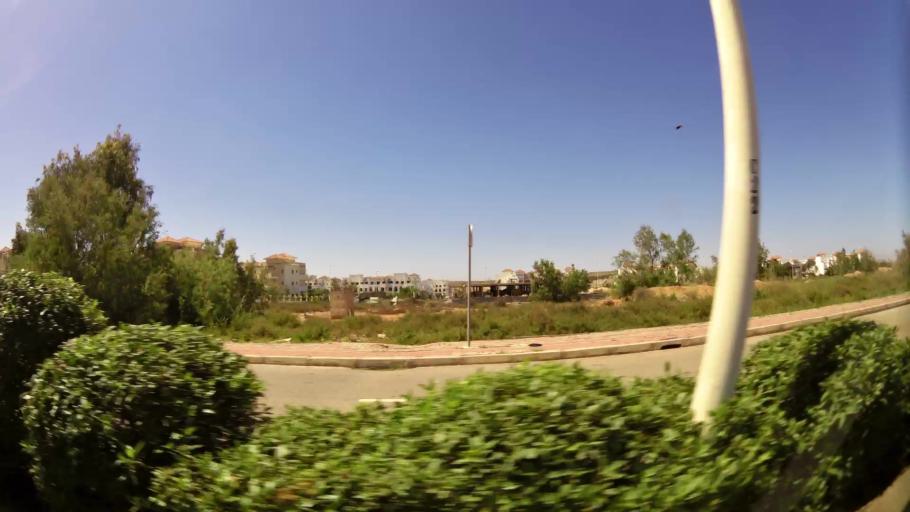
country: MA
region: Oriental
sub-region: Berkane-Taourirt
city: Madagh
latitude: 35.1031
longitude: -2.3061
